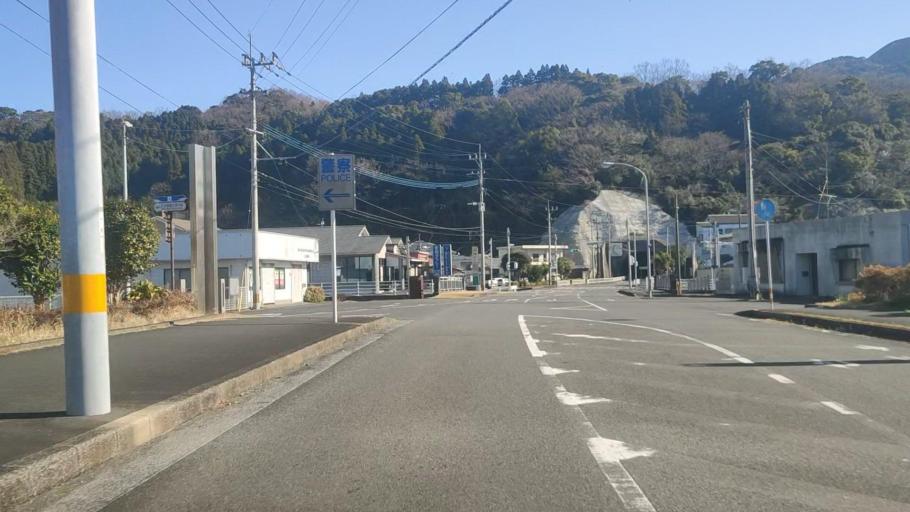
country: JP
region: Oita
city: Saiki
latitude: 32.8015
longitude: 131.9244
